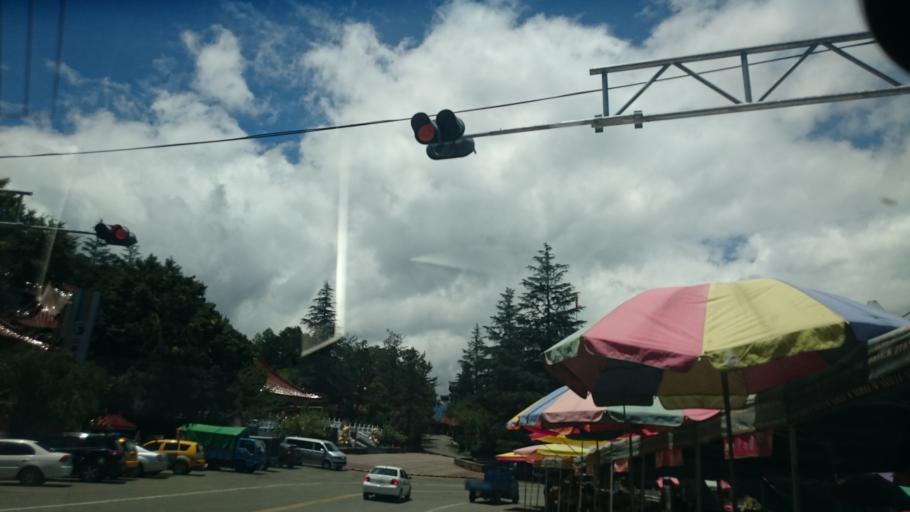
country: TW
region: Taiwan
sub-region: Nantou
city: Puli
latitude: 24.2542
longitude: 121.2524
